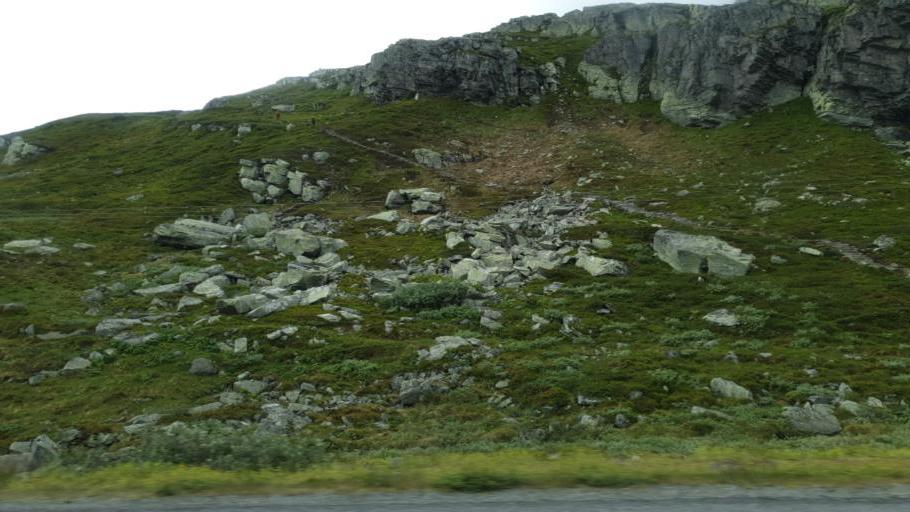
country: NO
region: Oppland
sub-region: Vestre Slidre
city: Slidre
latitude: 61.2894
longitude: 8.8131
